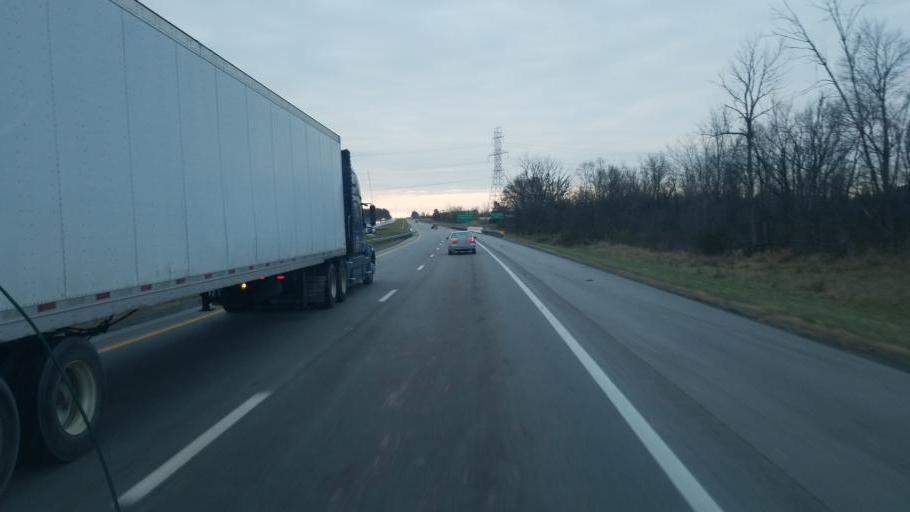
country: US
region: Ohio
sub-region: Allen County
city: Fort Shawnee
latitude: 40.6736
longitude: -84.1315
